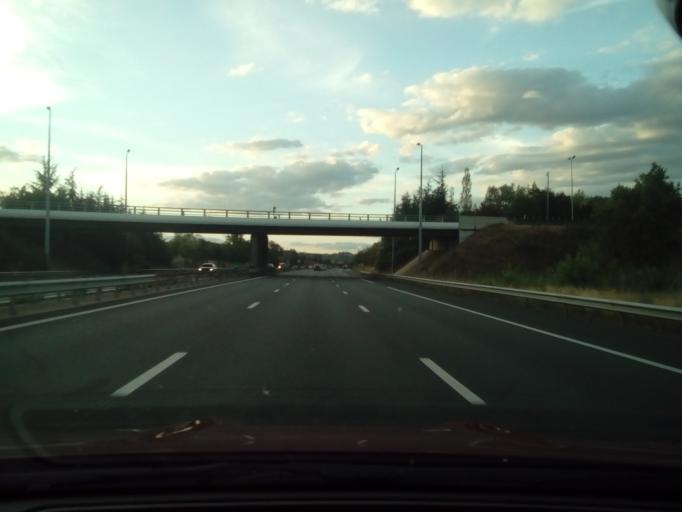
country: FR
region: Rhone-Alpes
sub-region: Departement de l'Isere
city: Chasse-sur-Rhone
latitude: 45.5897
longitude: 4.7980
